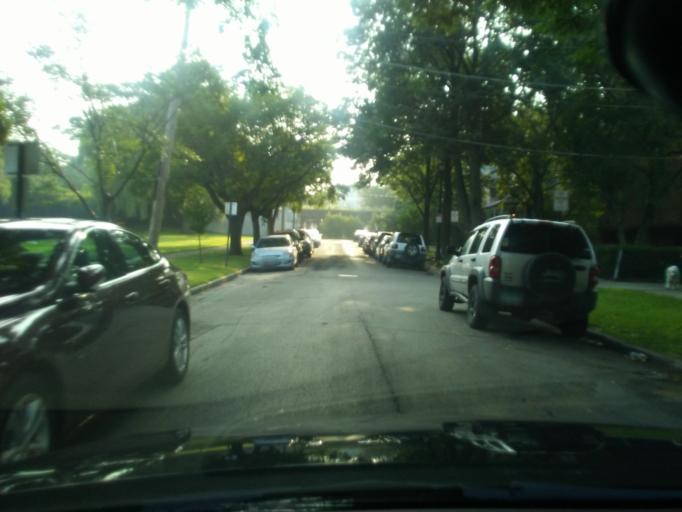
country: US
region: Illinois
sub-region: Cook County
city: Evanston
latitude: 42.0229
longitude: -87.6789
